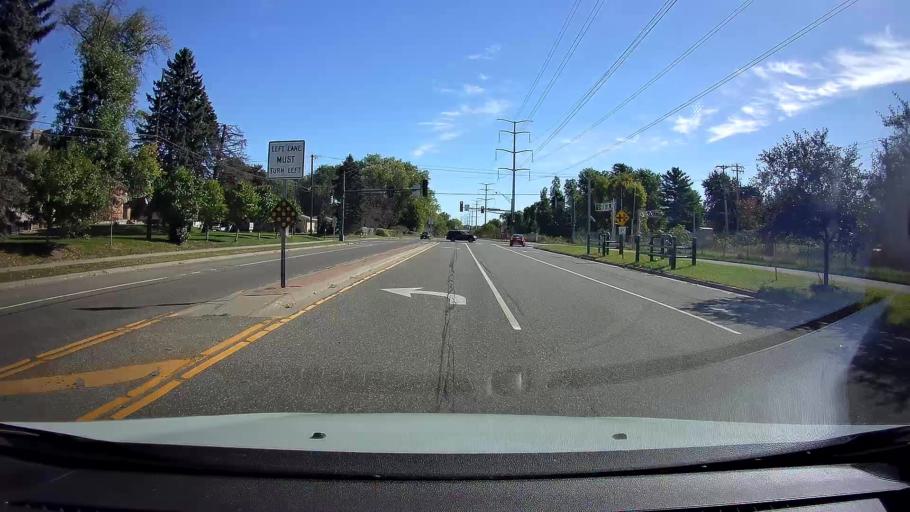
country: US
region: Minnesota
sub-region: Ramsey County
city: Roseville
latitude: 45.0207
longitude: -93.1578
